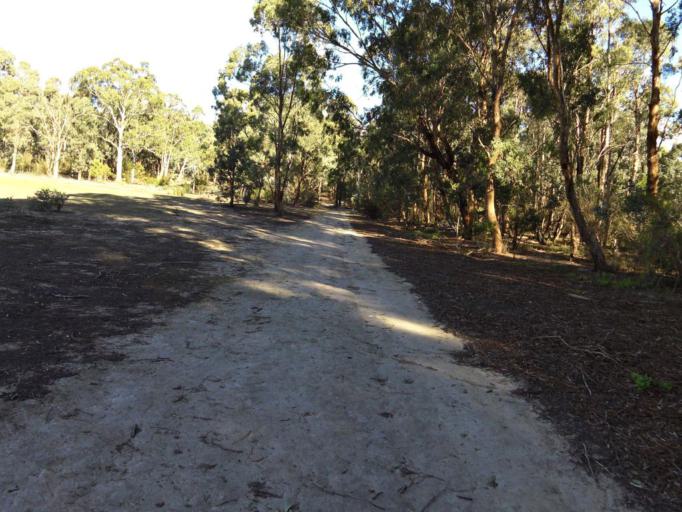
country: AU
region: Victoria
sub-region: Nillumbik
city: North Warrandyte
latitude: -37.7318
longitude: 145.2094
